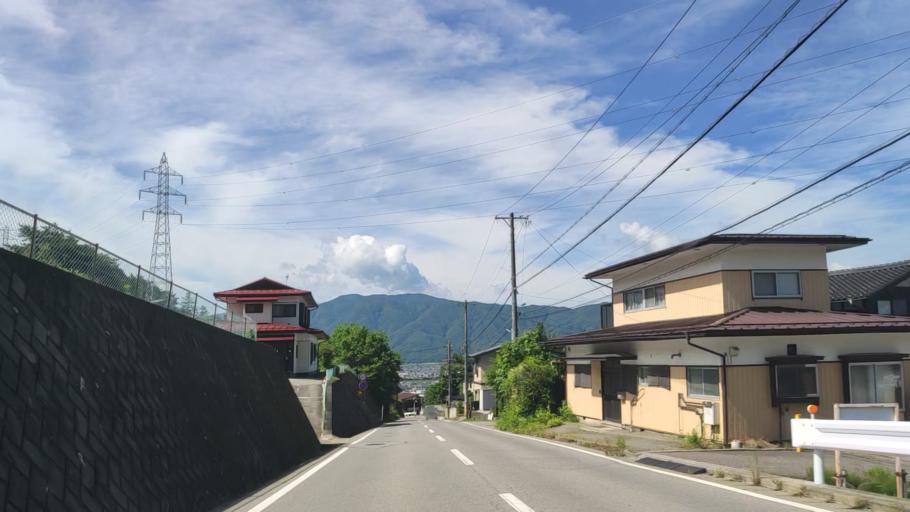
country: JP
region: Nagano
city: Suwa
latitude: 36.0456
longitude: 138.1274
